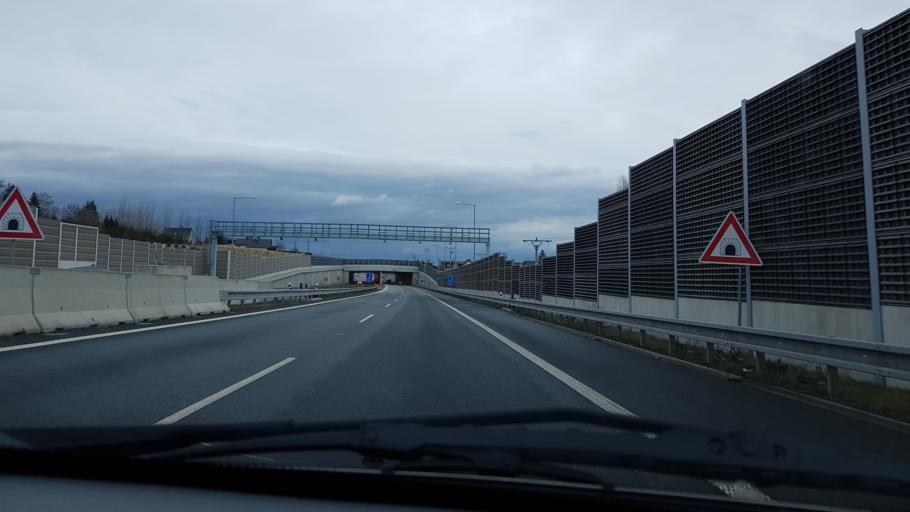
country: CZ
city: Staric
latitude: 49.6655
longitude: 18.2944
